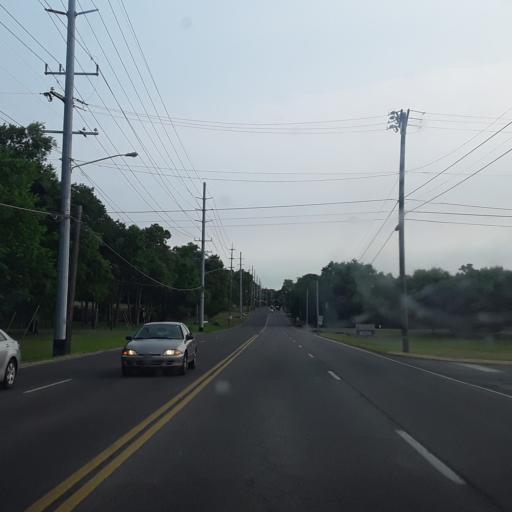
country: US
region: Tennessee
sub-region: Davidson County
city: Oak Hill
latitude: 36.0631
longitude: -86.7742
